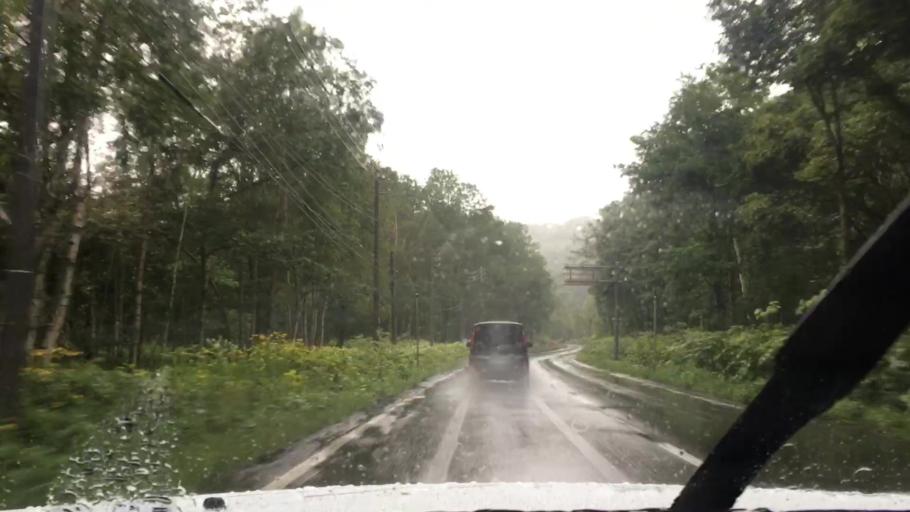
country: JP
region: Hokkaido
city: Otaru
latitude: 42.8455
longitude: 141.0205
